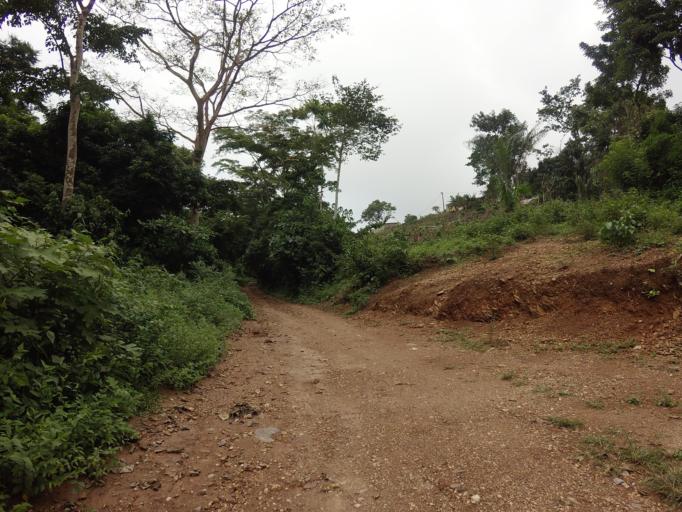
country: TG
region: Plateaux
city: Kpalime
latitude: 6.8447
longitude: 0.4400
